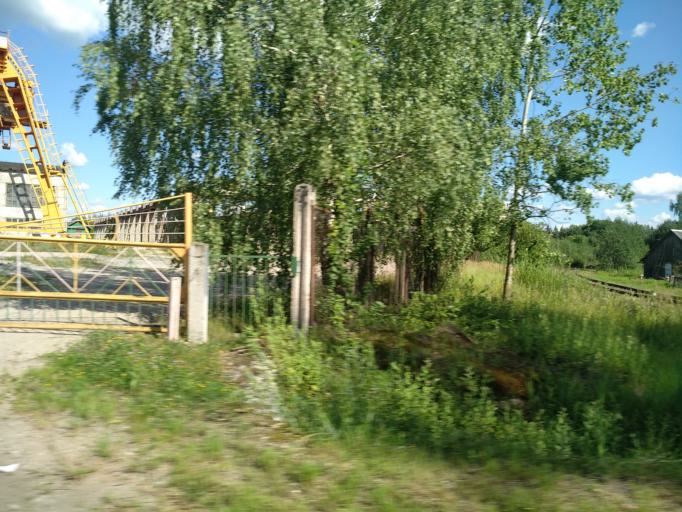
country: BY
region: Vitebsk
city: Mosar
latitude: 55.1236
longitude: 27.2109
